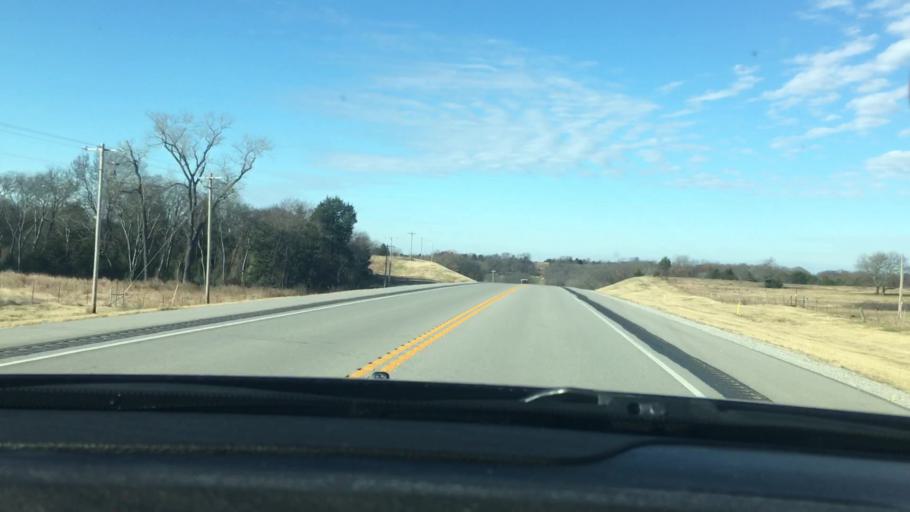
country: US
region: Oklahoma
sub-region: Love County
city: Marietta
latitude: 33.9404
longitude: -97.2514
